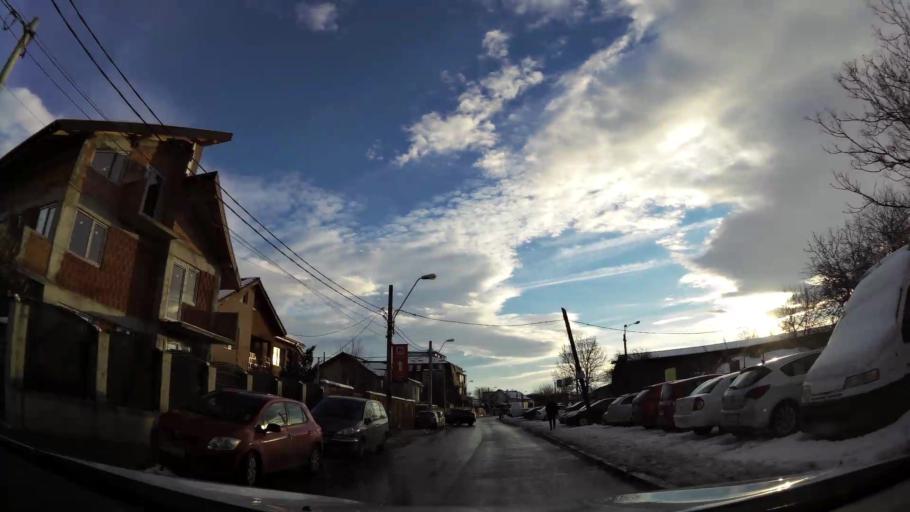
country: RO
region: Ilfov
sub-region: Comuna Popesti-Leordeni
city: Popesti-Leordeni
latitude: 44.3776
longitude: 26.1331
